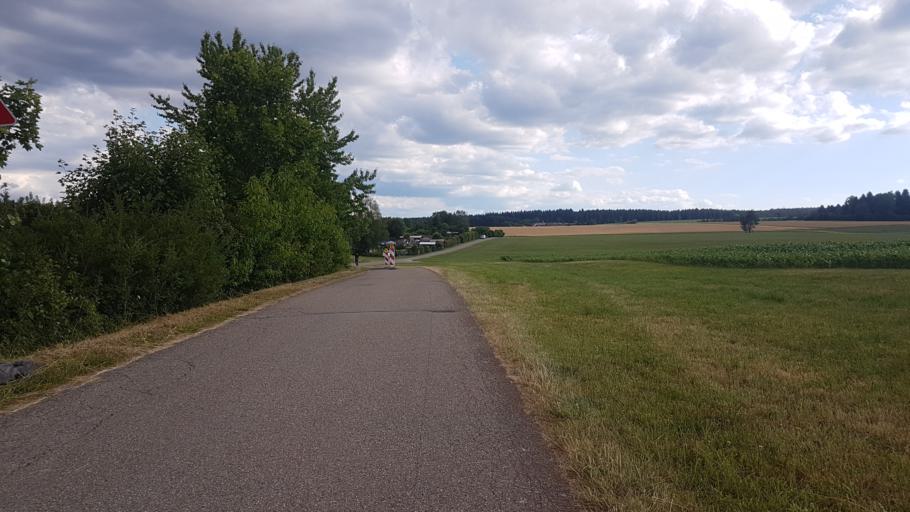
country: DE
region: Baden-Wuerttemberg
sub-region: Freiburg Region
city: Unterkirnach
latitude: 48.0358
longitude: 8.4106
